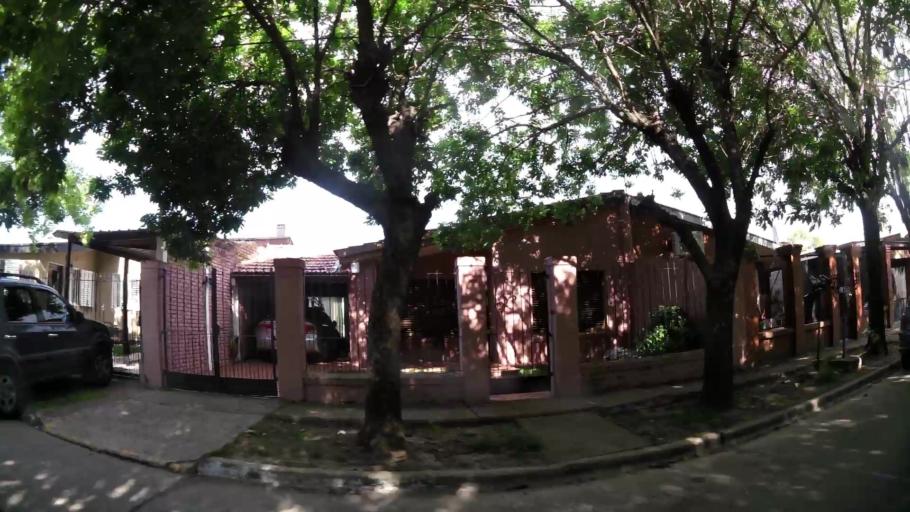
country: AR
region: Buenos Aires
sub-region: Partido de Almirante Brown
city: Adrogue
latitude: -34.8192
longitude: -58.3505
